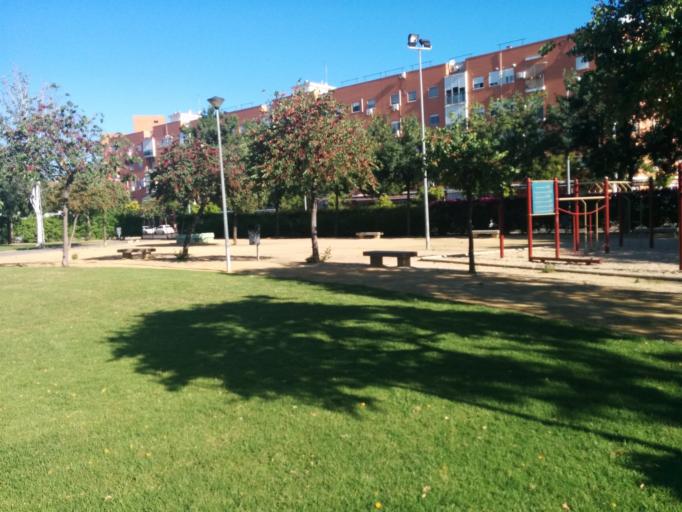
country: ES
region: Andalusia
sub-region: Provincia de Sevilla
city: Sevilla
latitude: 37.4096
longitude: -5.9151
